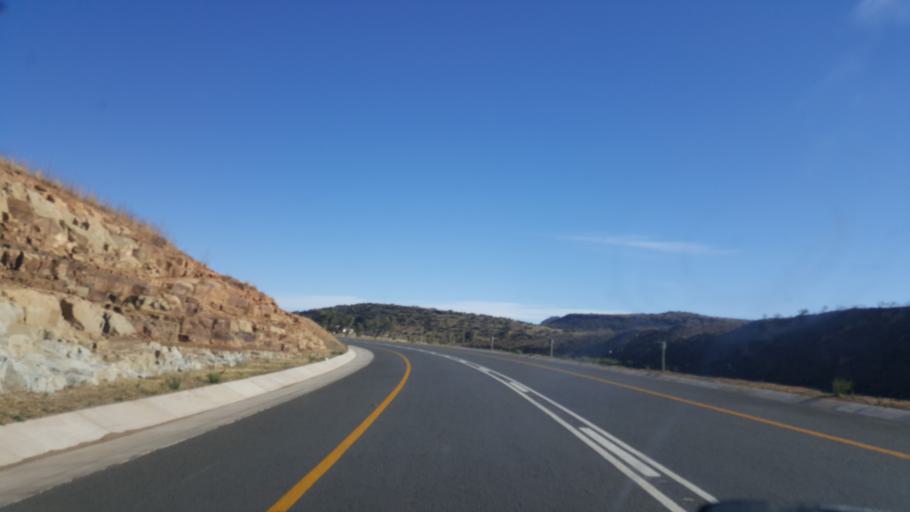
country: ZA
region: Eastern Cape
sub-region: Chris Hani District Municipality
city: Middelburg
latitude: -31.3774
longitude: 25.0341
